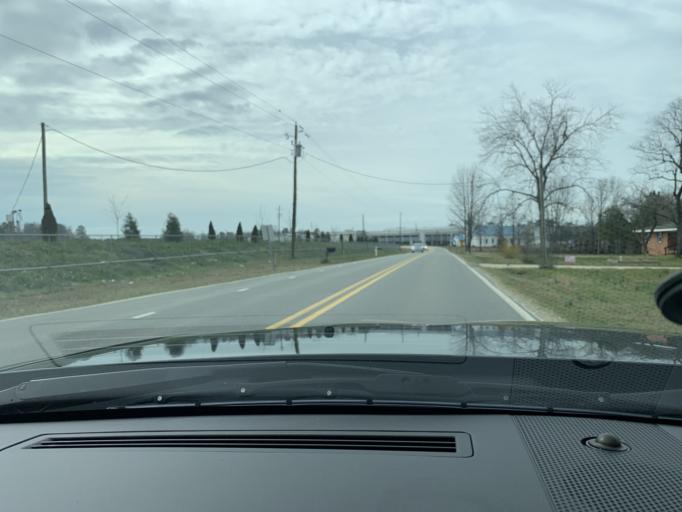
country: US
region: North Carolina
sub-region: Johnston County
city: Clayton
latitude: 35.6204
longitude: -78.4049
